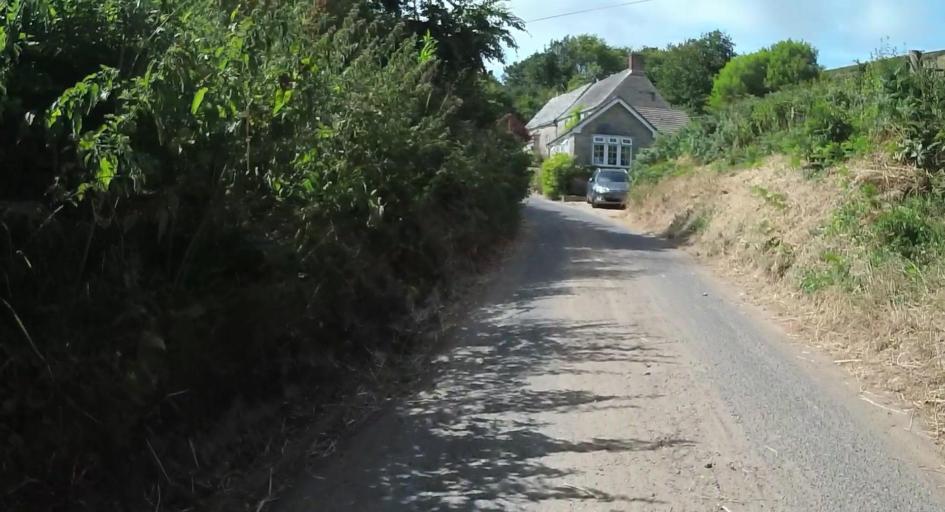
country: GB
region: England
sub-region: Dorset
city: Swanage
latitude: 50.6302
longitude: -2.0097
